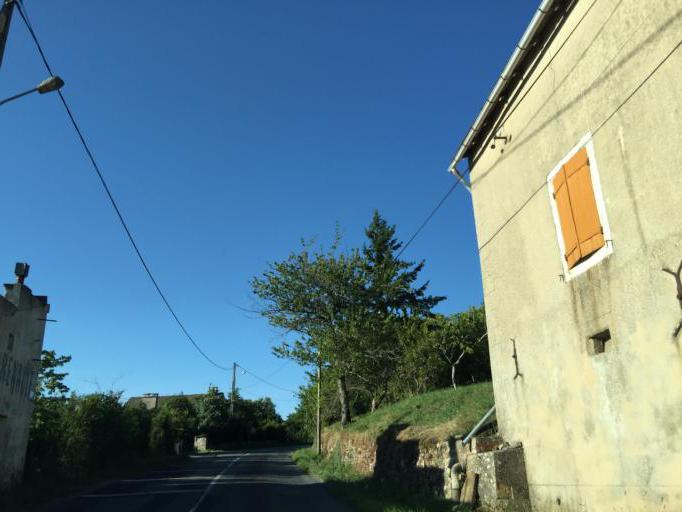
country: FR
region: Midi-Pyrenees
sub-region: Departement de l'Aveyron
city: Saint-Georges-de-Luzencon
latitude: 44.1036
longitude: 2.8999
